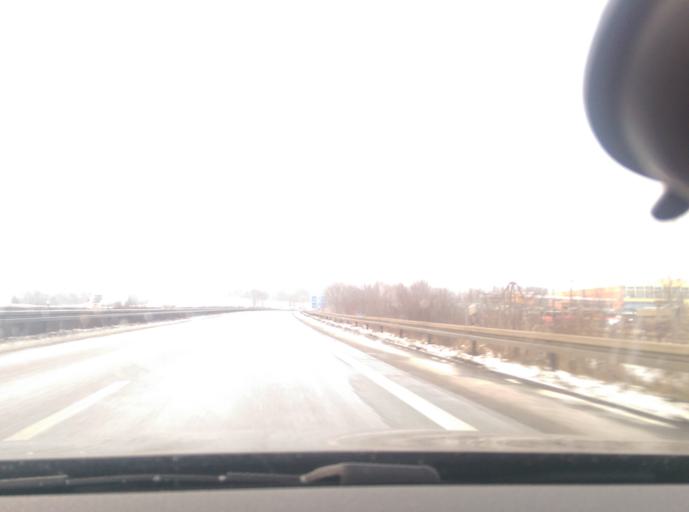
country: DE
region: Hesse
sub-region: Regierungsbezirk Kassel
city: Fuldabruck
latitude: 51.2793
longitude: 9.4769
